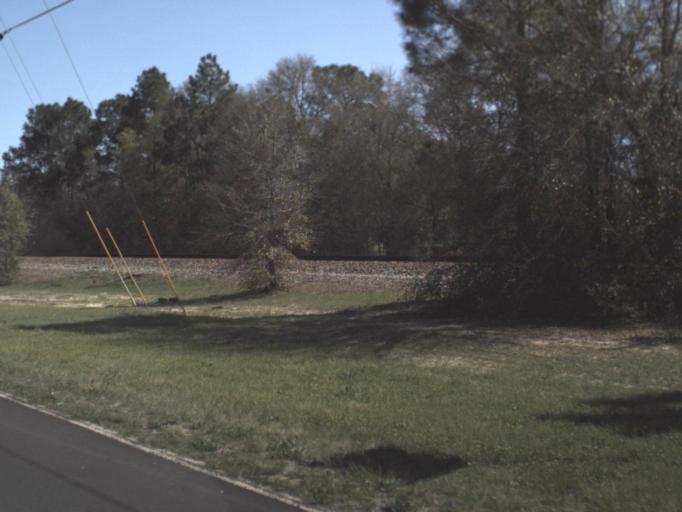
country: US
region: Florida
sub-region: Walton County
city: DeFuniak Springs
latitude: 30.7318
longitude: -86.1416
